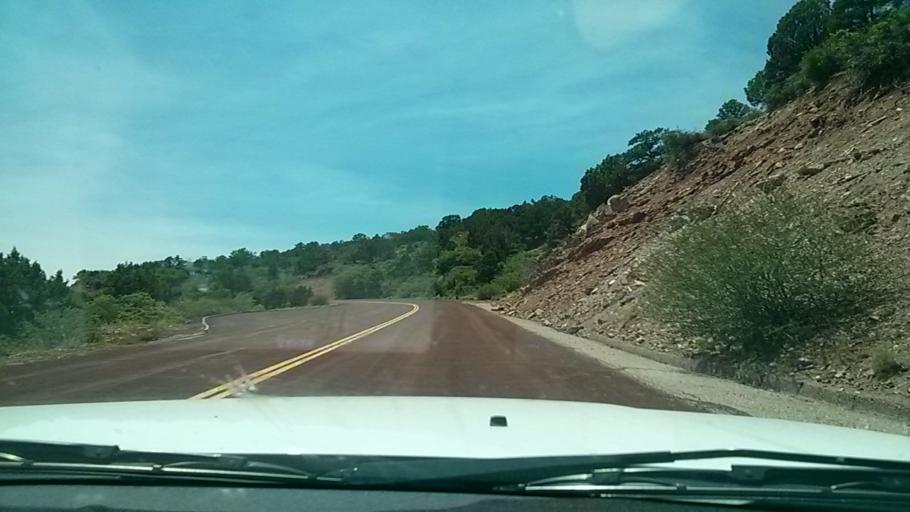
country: US
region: Utah
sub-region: Washington County
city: Toquerville
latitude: 37.4377
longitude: -113.1976
